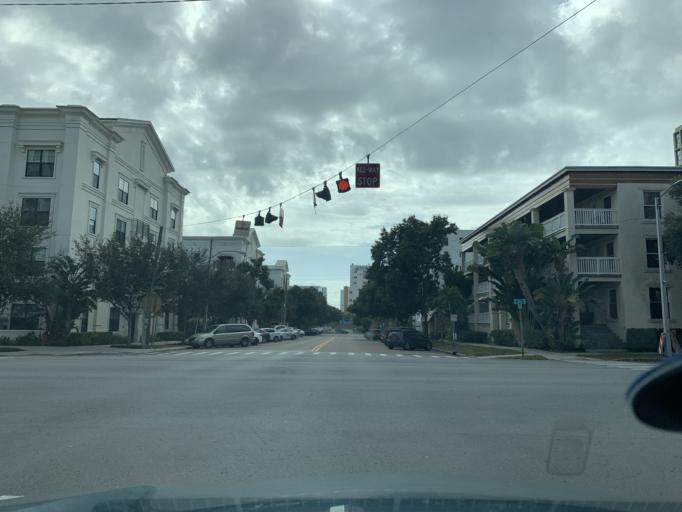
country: US
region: Florida
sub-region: Pinellas County
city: Saint Petersburg
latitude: 27.7687
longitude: -82.6402
